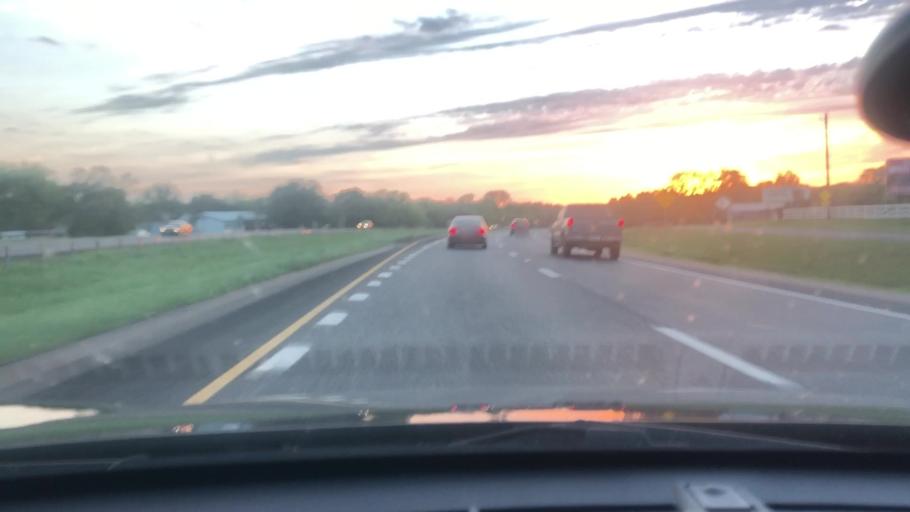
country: US
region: Texas
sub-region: Jackson County
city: Edna
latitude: 28.9607
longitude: -96.6821
